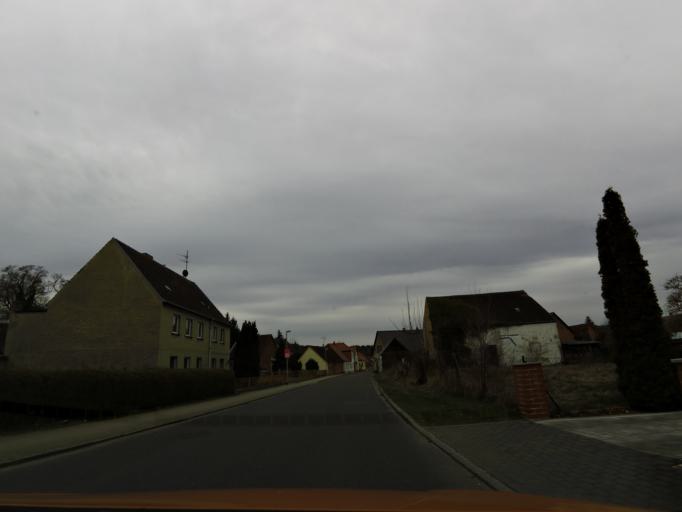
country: DE
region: Brandenburg
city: Belzig
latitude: 52.1406
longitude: 12.5926
